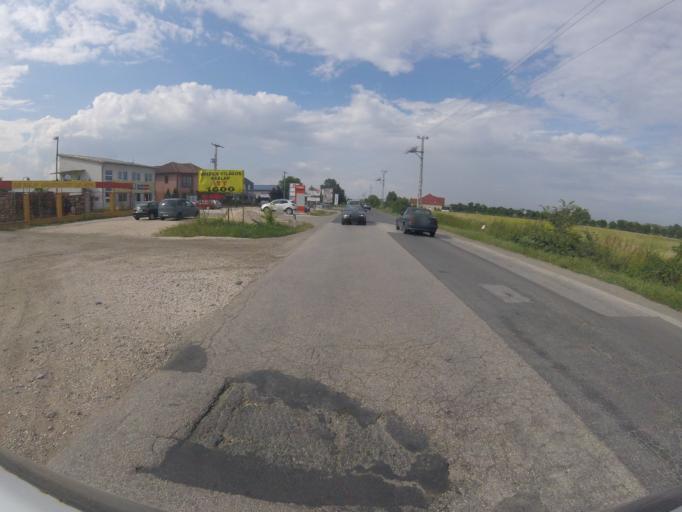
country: HU
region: Pest
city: Szigetszentmiklos
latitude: 47.3842
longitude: 19.0496
